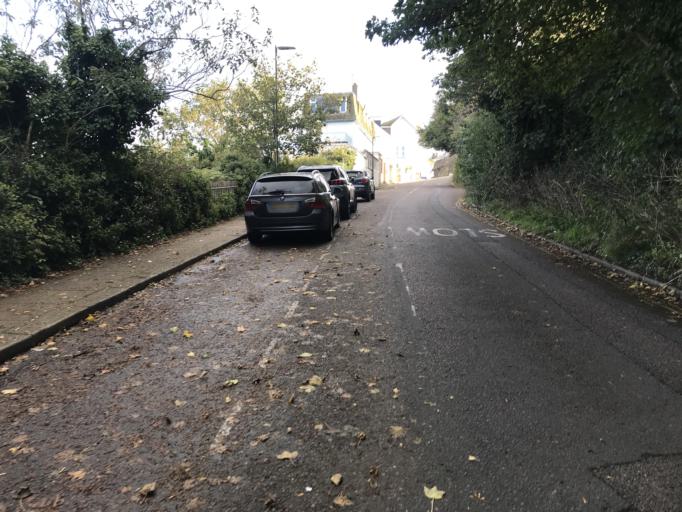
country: GB
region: England
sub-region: Borough of Torbay
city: Brixham
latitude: 50.3989
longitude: -3.5150
